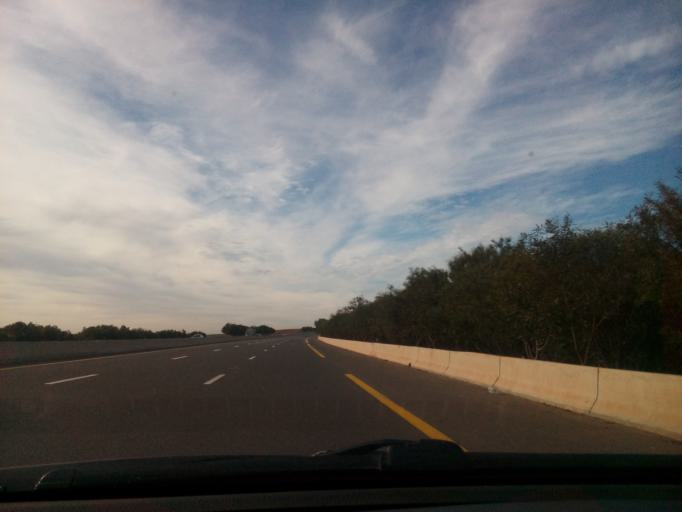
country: DZ
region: Sidi Bel Abbes
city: Sidi Bel Abbes
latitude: 35.1959
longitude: -0.6973
